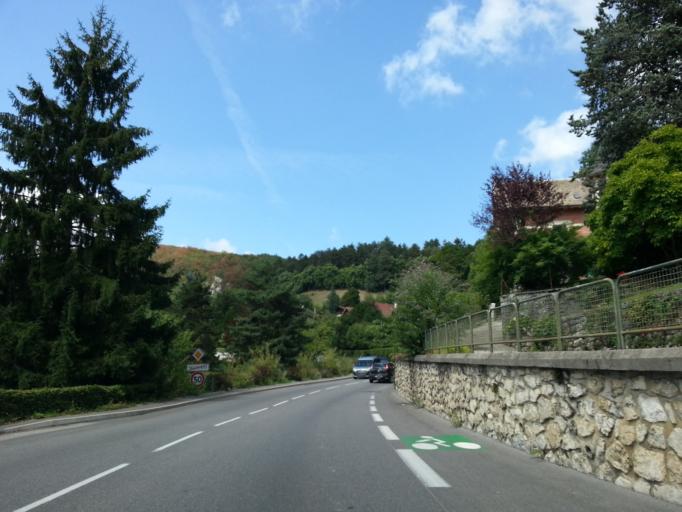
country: FR
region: Rhone-Alpes
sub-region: Departement de la Haute-Savoie
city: Talloires
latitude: 45.8428
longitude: 6.2134
